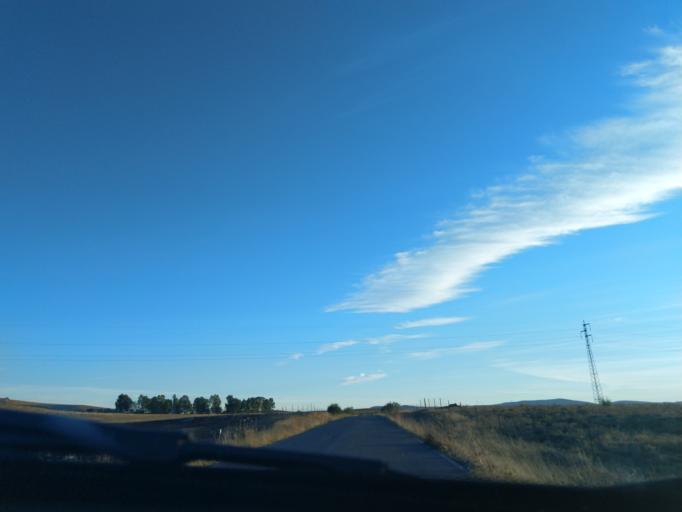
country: ES
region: Extremadura
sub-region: Provincia de Badajoz
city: Ahillones
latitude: 38.2600
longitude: -5.8262
